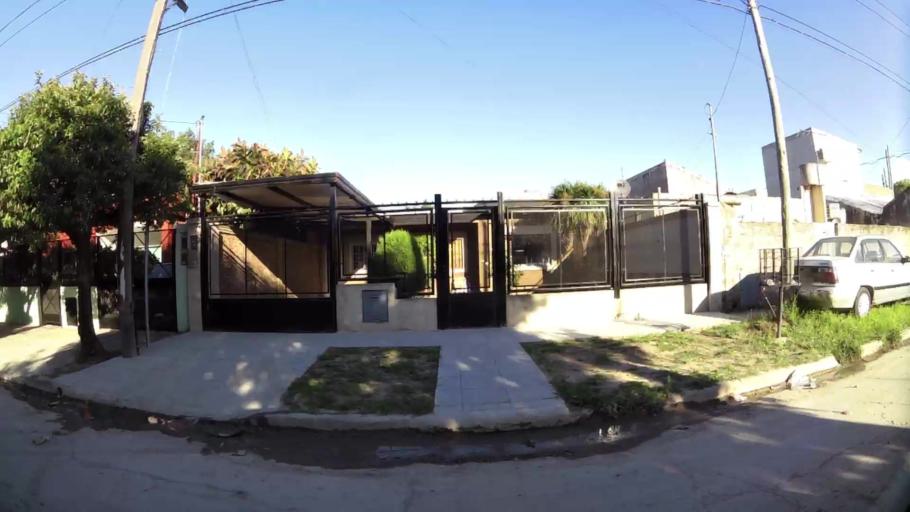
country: AR
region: Buenos Aires
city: Ituzaingo
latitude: -34.6866
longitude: -58.6390
